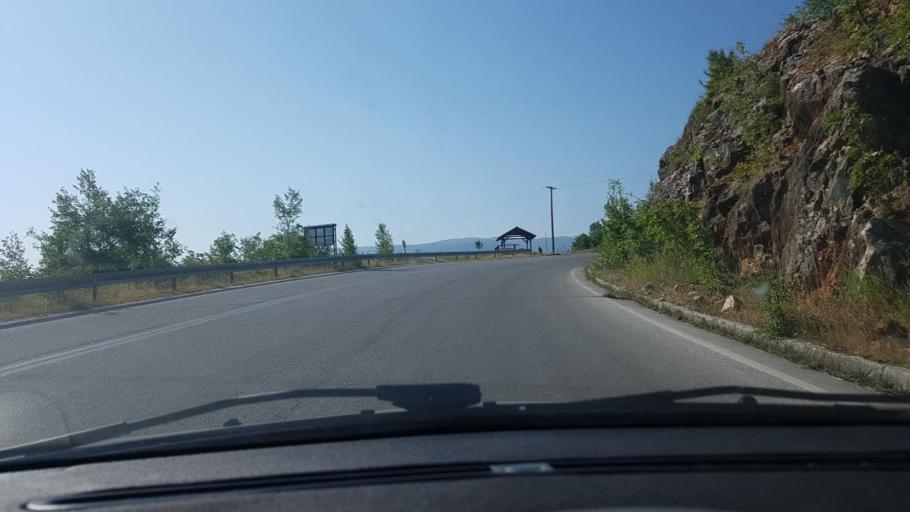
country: BA
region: Federation of Bosnia and Herzegovina
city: Rumboci
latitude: 43.8215
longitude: 17.4747
